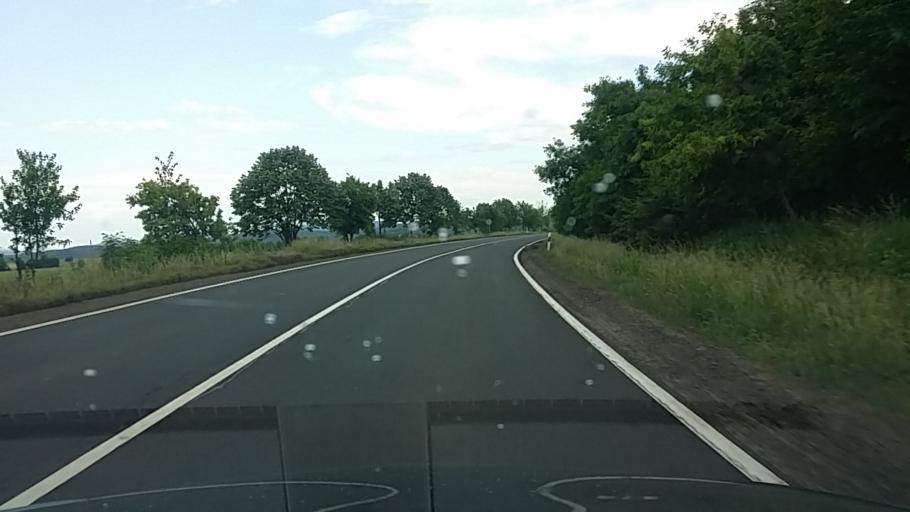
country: HU
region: Nograd
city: Nagyoroszi
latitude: 47.9863
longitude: 19.1127
